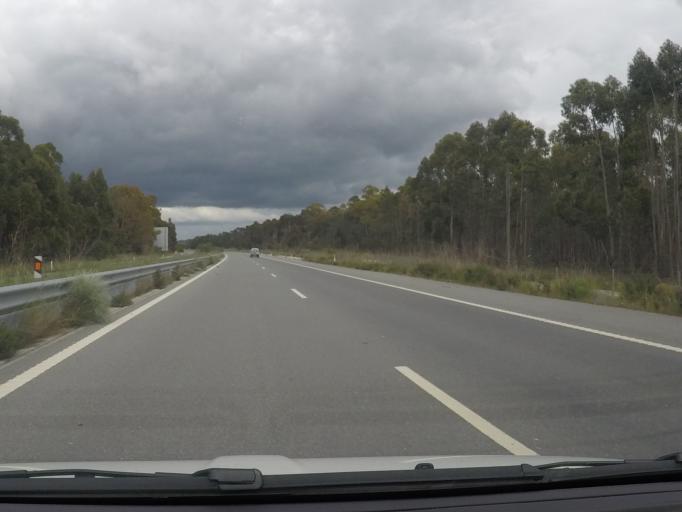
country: PT
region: Setubal
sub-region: Sines
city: Sines
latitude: 37.9802
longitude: -8.7939
